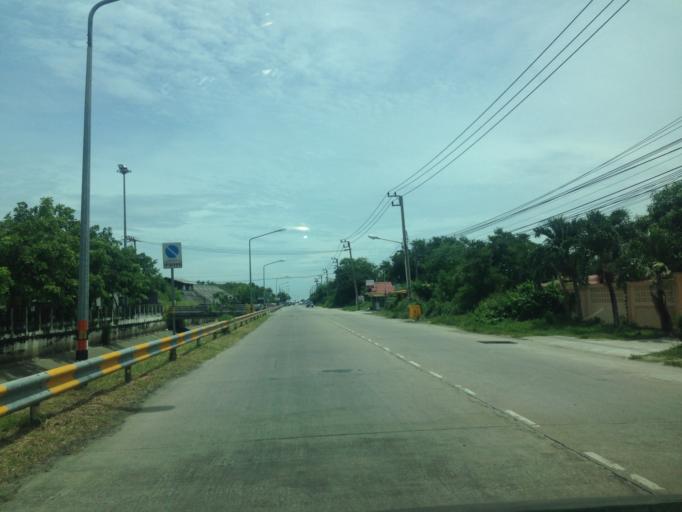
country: TH
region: Chon Buri
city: Chon Buri
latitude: 13.3744
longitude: 100.9828
